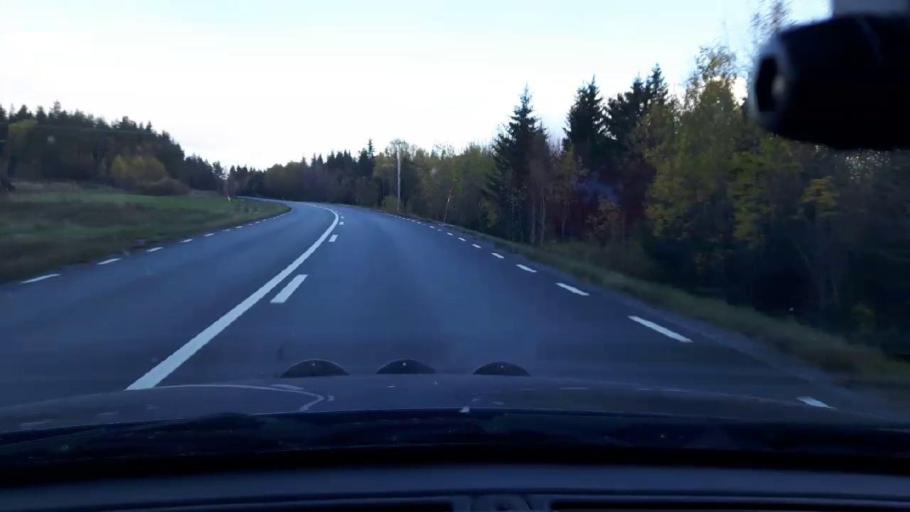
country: SE
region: Jaemtland
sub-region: Krokoms Kommun
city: Krokom
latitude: 63.0746
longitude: 14.2962
